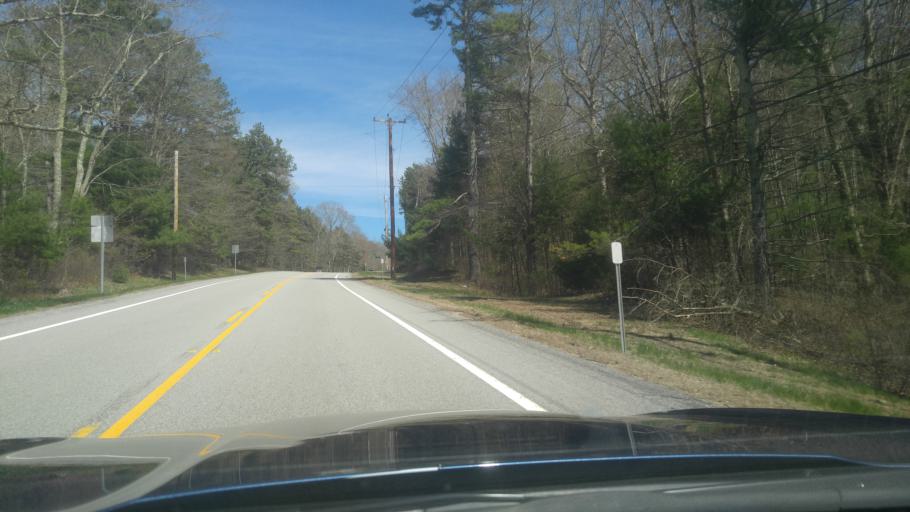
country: US
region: Rhode Island
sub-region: Washington County
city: Hope Valley
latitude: 41.5763
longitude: -71.7111
